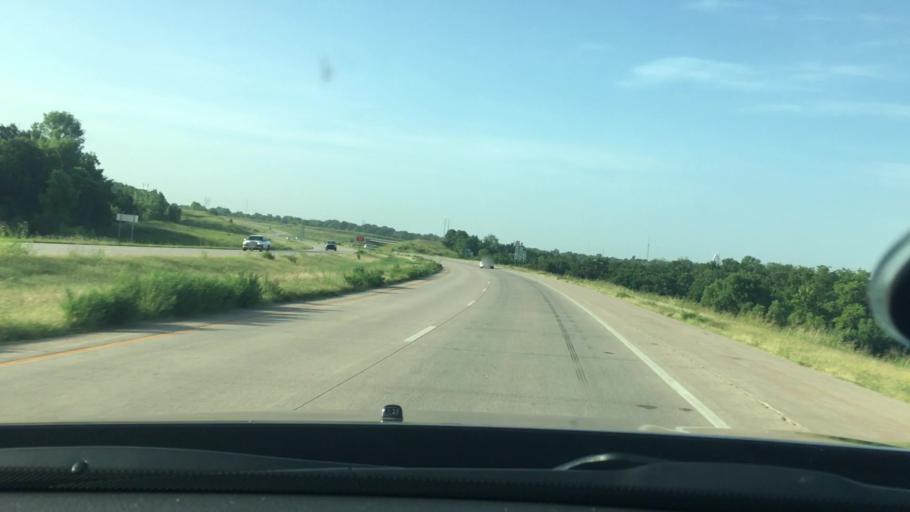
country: US
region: Oklahoma
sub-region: Pontotoc County
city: Ada
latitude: 34.7975
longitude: -96.6960
